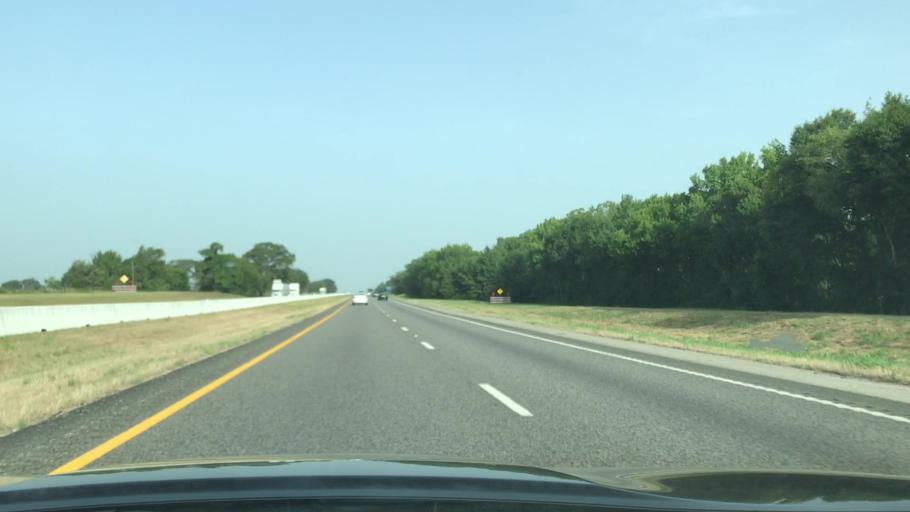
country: US
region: Texas
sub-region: Van Zandt County
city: Van
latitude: 32.5099
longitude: -95.6604
